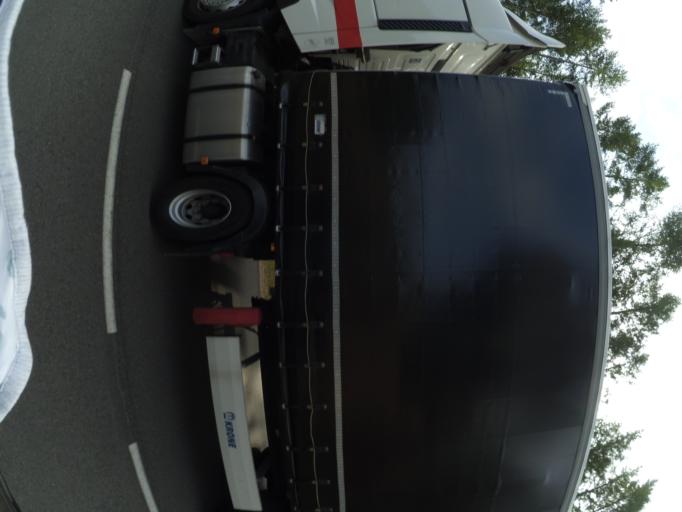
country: FR
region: Limousin
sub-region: Departement de la Correze
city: Meymac
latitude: 45.5751
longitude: 2.1363
